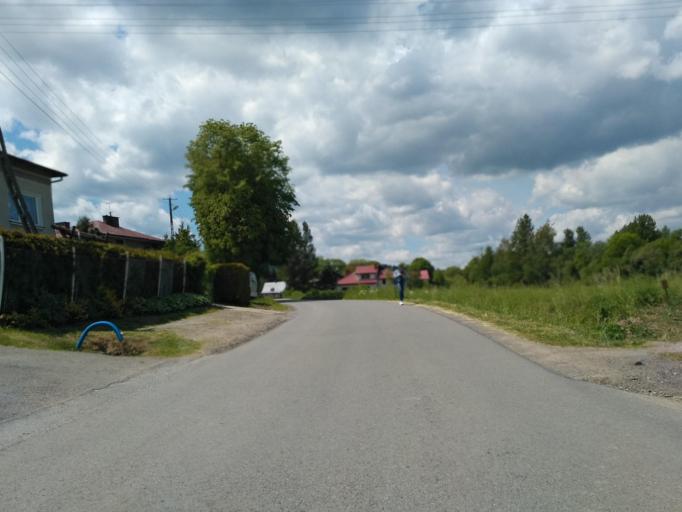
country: PL
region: Subcarpathian Voivodeship
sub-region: Powiat krosnienski
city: Dukla
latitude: 49.5549
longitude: 21.6713
